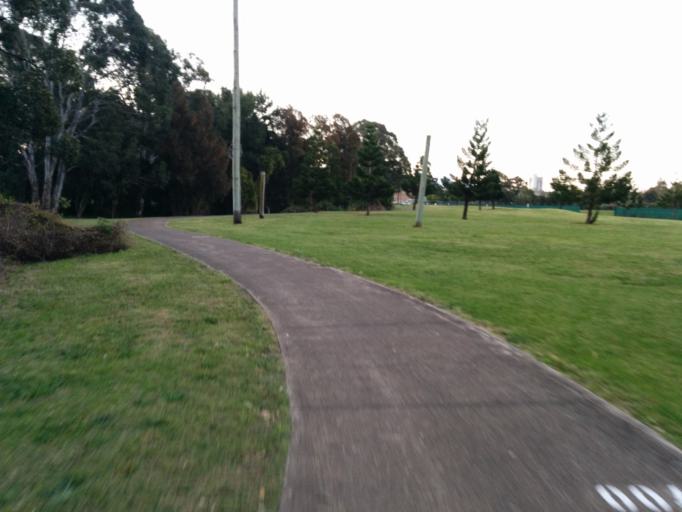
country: AU
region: New South Wales
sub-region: Fairfield
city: Fairfield Heights
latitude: -33.8520
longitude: 150.9457
